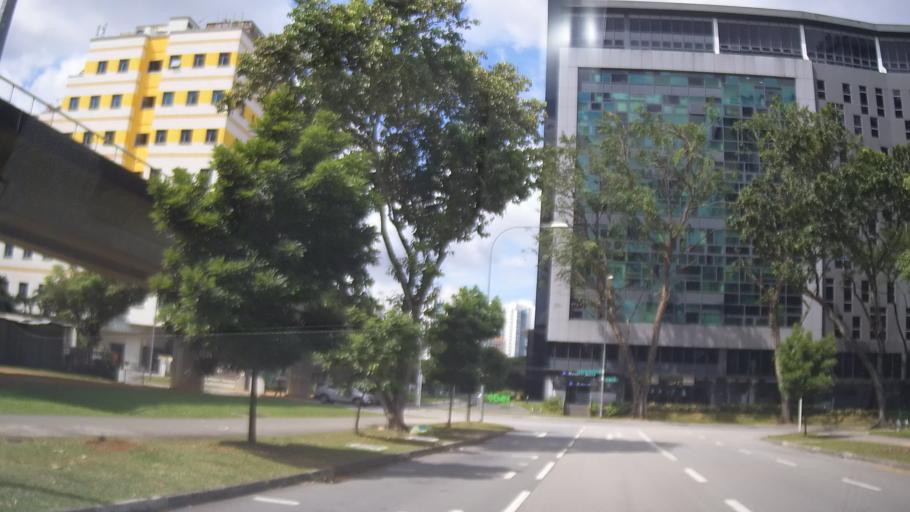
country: SG
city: Singapore
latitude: 1.3159
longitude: 103.8786
